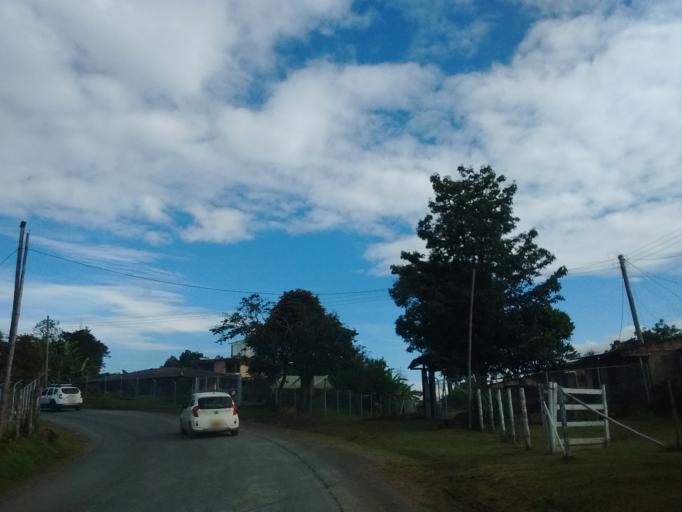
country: CO
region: Cauca
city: Cajibio
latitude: 2.6028
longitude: -76.5287
